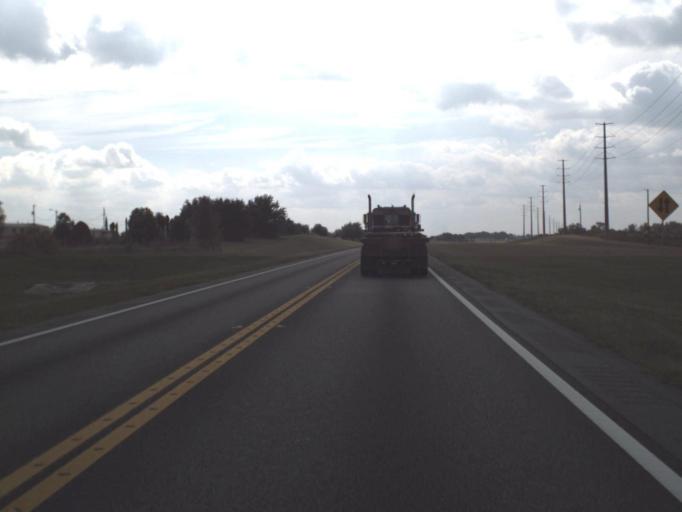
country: US
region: Florida
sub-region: Polk County
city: Auburndale
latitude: 28.1009
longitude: -81.8302
